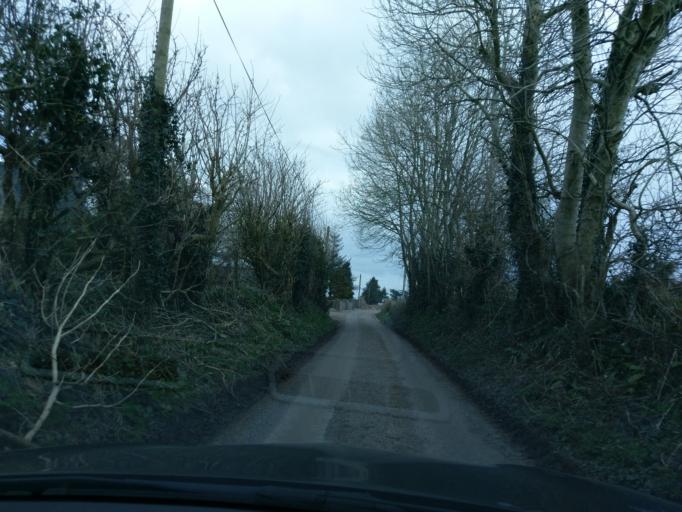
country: IE
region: Connaught
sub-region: County Galway
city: Athenry
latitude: 53.4503
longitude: -8.6632
